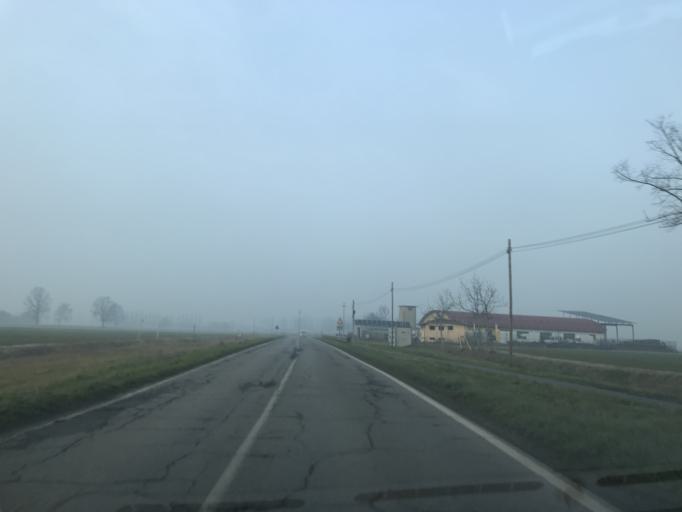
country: IT
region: Lombardy
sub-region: Provincia di Lodi
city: Ossago Lodigiano
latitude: 45.2530
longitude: 9.5360
